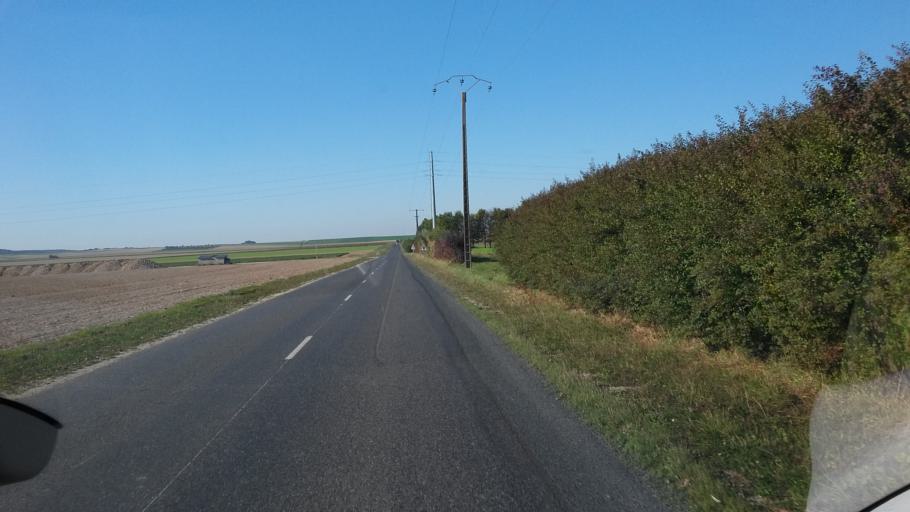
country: FR
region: Champagne-Ardenne
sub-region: Departement de la Marne
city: Connantre
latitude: 48.7381
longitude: 3.8992
